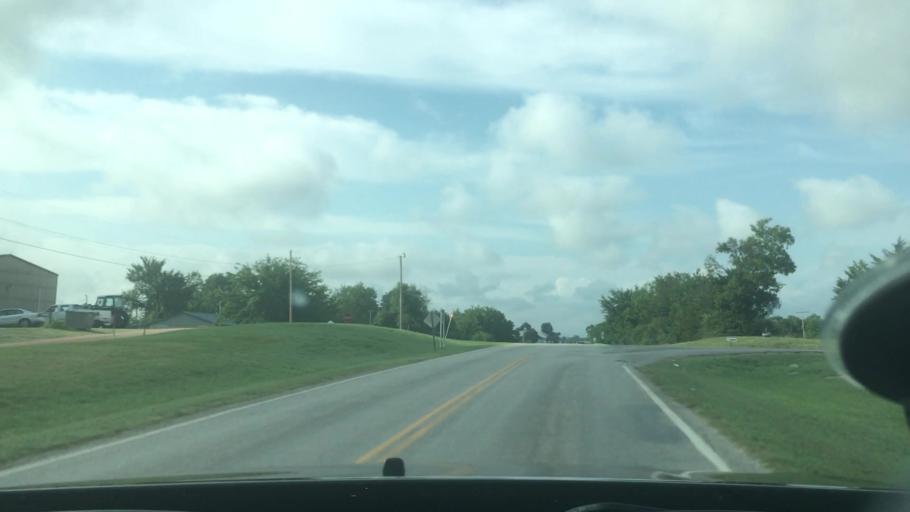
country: US
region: Oklahoma
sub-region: Pontotoc County
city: Ada
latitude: 34.6514
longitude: -96.5301
